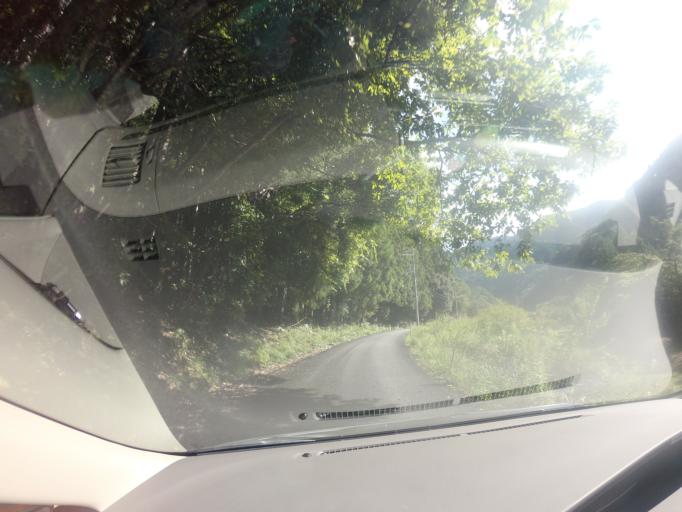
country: JP
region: Wakayama
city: Shingu
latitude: 33.9685
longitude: 135.8452
